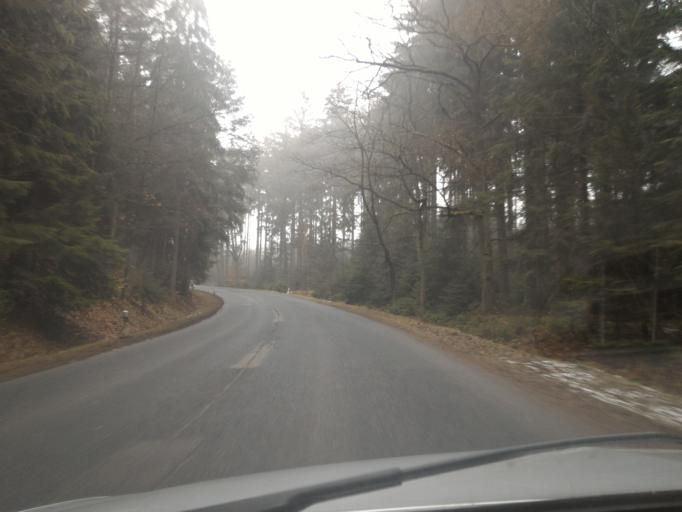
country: PL
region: Lower Silesian Voivodeship
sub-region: Powiat zgorzelecki
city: Bogatynia
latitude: 50.9103
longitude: 15.0069
